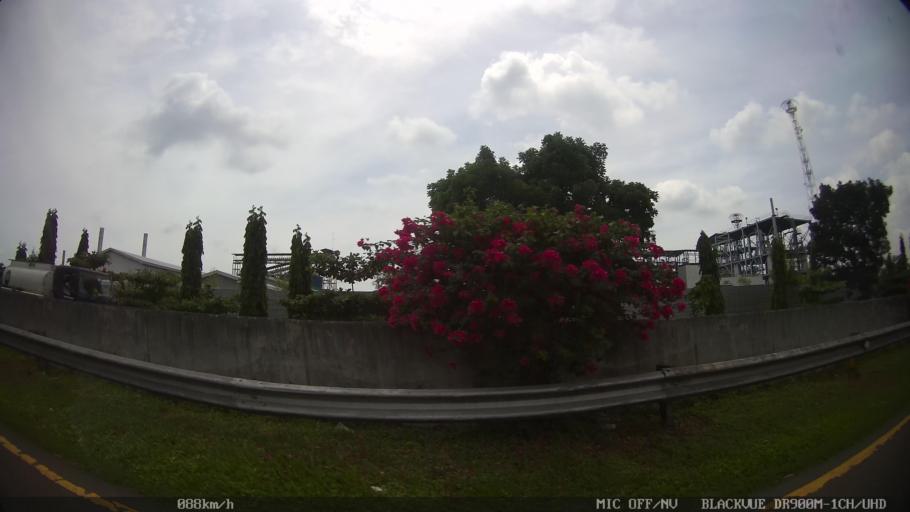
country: ID
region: North Sumatra
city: Labuhan Deli
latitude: 3.6814
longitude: 98.6807
